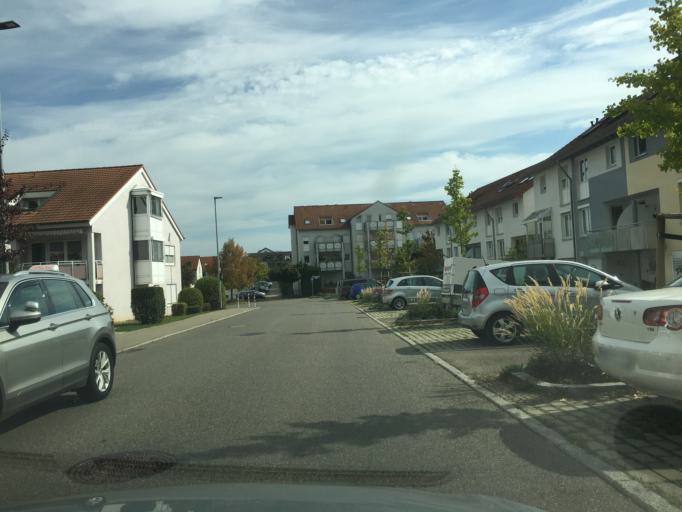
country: DE
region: Baden-Wuerttemberg
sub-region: Regierungsbezirk Stuttgart
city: Boeblingen
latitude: 48.6675
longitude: 9.0000
